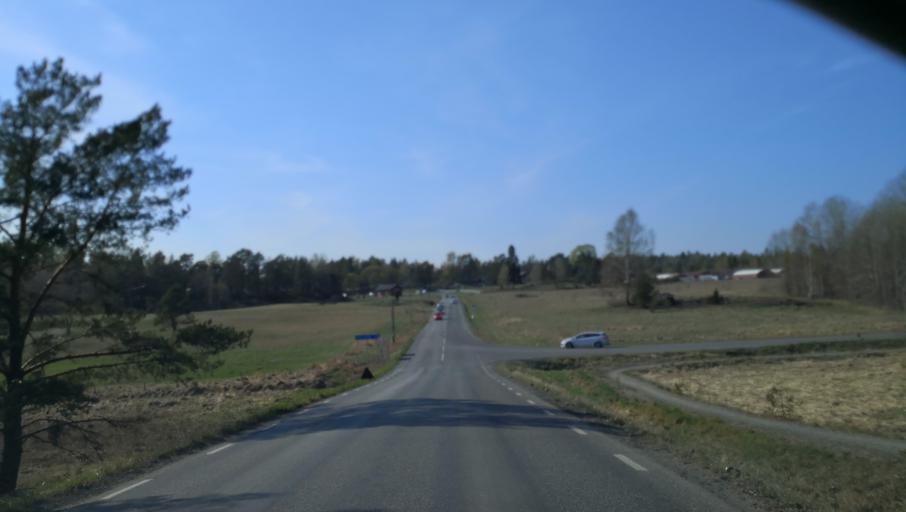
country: SE
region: Stockholm
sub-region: Varmdo Kommun
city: Hemmesta
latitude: 59.3244
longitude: 18.5480
